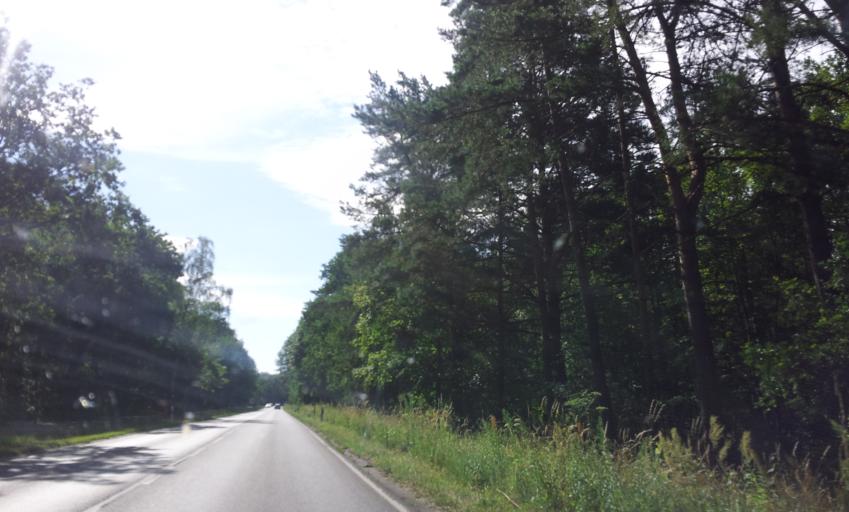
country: DE
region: Berlin
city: Friedrichshagen
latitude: 52.4321
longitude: 13.6095
